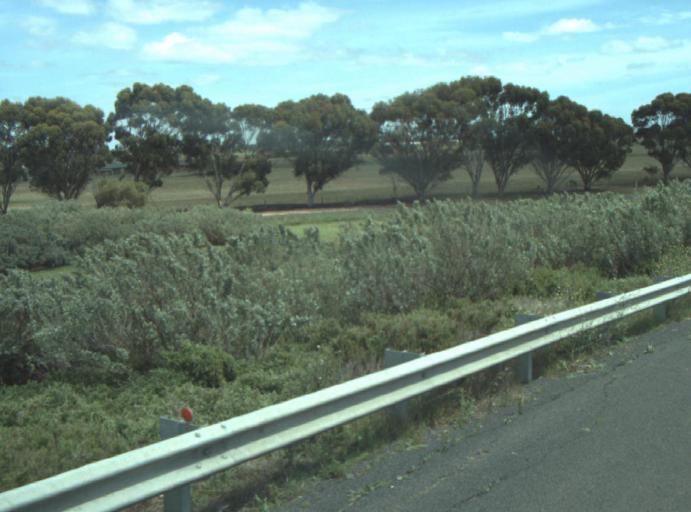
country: AU
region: Victoria
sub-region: Wyndham
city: Little River
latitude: -38.0131
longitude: 144.4662
